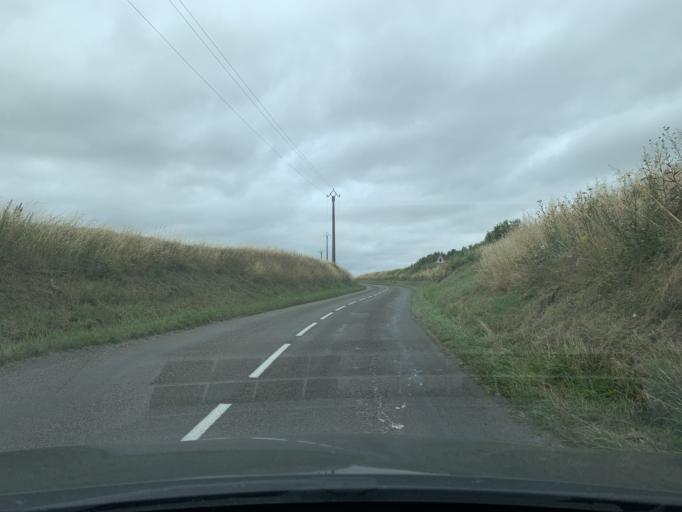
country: FR
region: Nord-Pas-de-Calais
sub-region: Departement du Nord
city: Neuville-Saint-Remy
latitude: 50.2261
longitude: 3.2178
